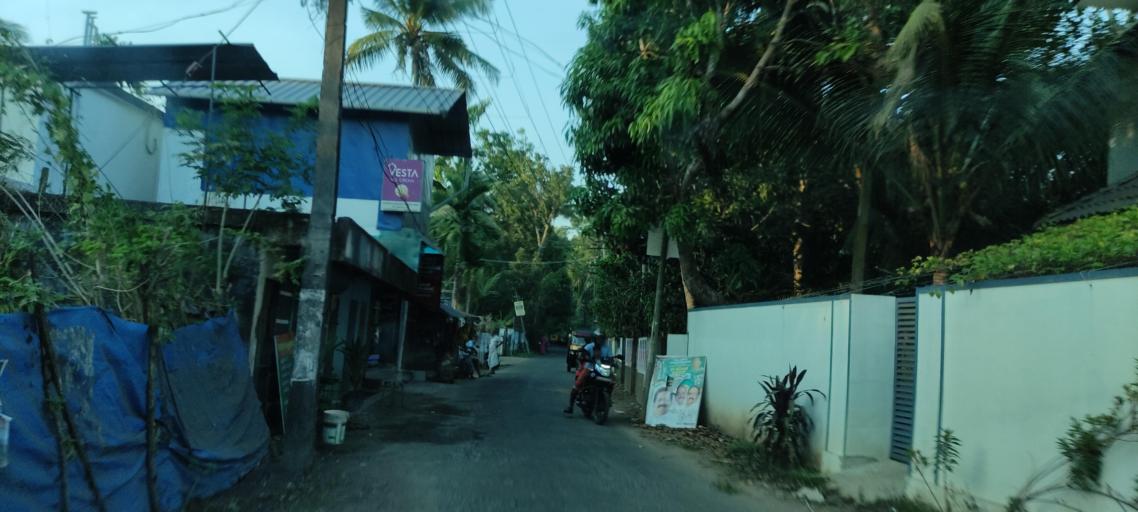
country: IN
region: Kerala
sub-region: Alappuzha
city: Kutiatodu
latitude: 9.7762
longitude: 76.3251
